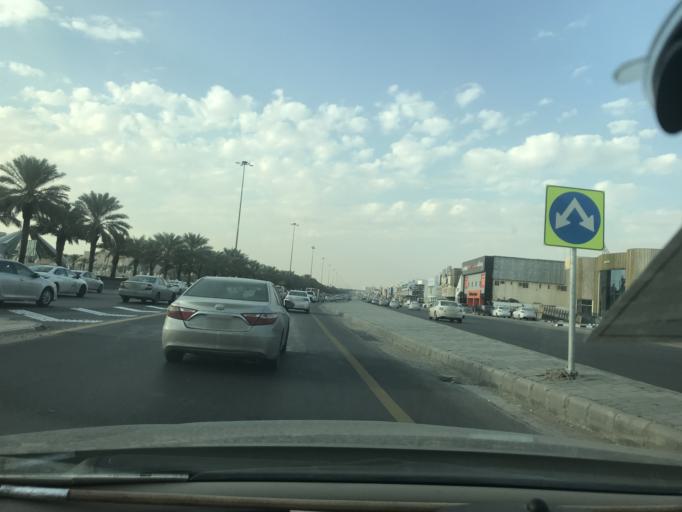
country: SA
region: Ar Riyad
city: Riyadh
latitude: 24.7421
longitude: 46.7481
